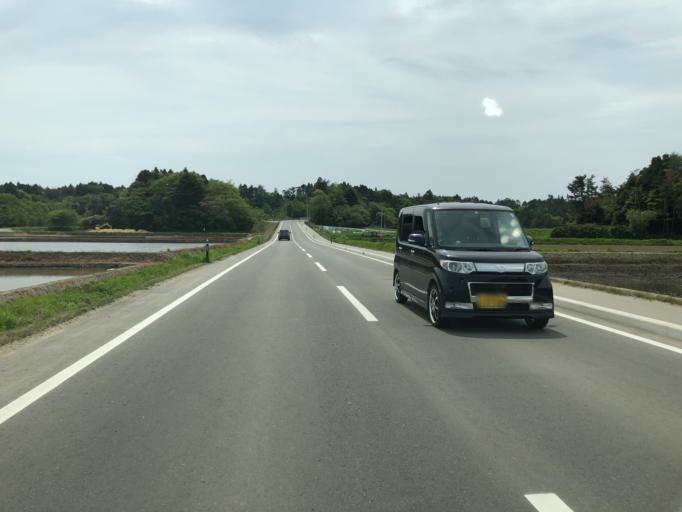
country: JP
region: Fukushima
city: Namie
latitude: 37.7131
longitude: 141.0060
